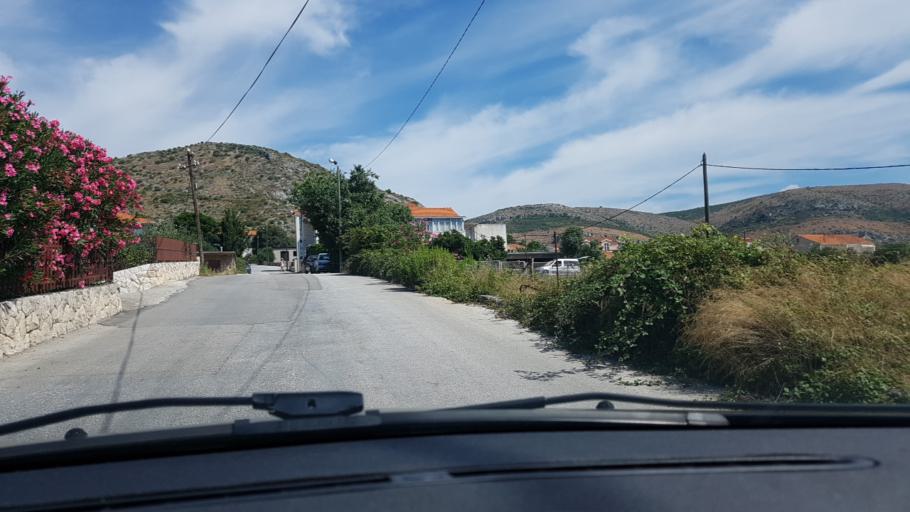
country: HR
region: Splitsko-Dalmatinska
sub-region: Grad Trogir
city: Trogir
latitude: 43.5206
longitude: 16.2278
